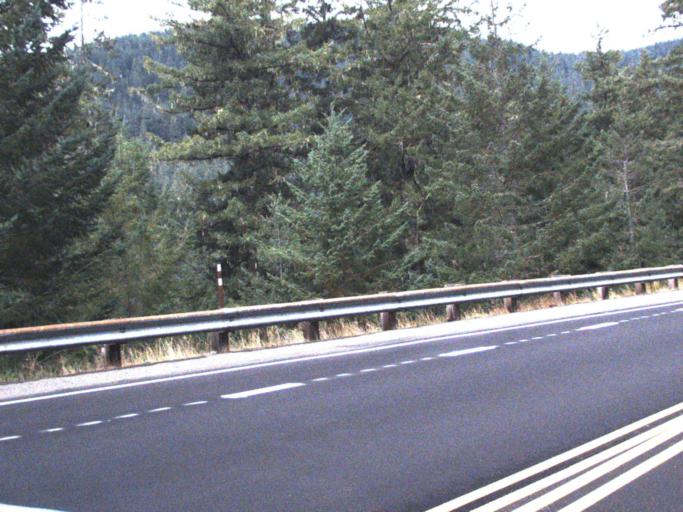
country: US
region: Washington
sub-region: Pierce County
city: Buckley
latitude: 46.6866
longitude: -121.5791
